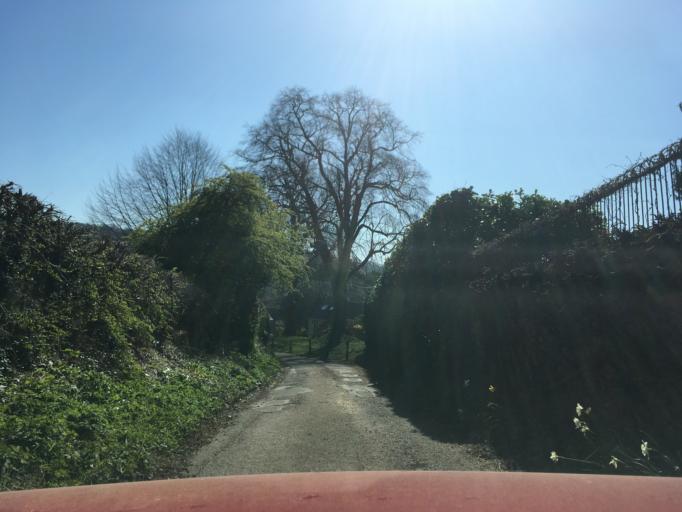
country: GB
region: England
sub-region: Gloucestershire
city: Wotton-under-Edge
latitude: 51.6412
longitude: -2.3492
